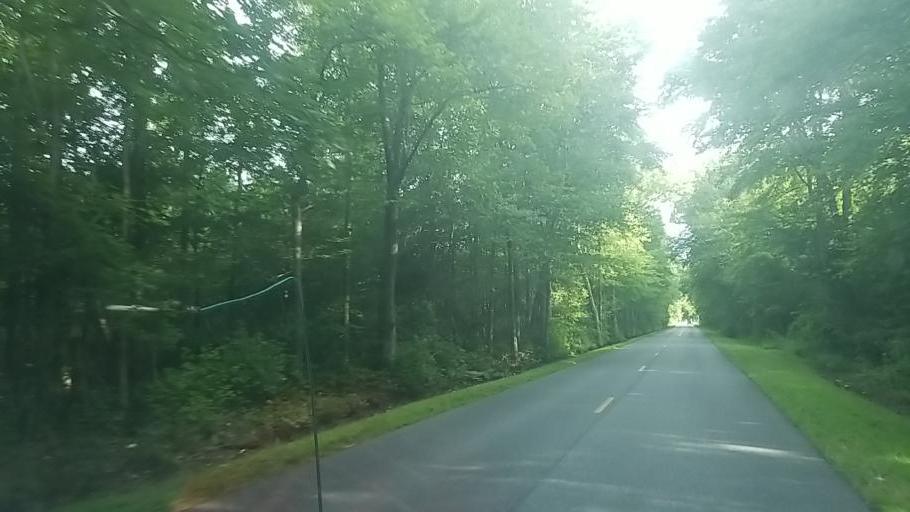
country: US
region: Maryland
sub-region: Worcester County
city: West Ocean City
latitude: 38.3363
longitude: -75.1560
